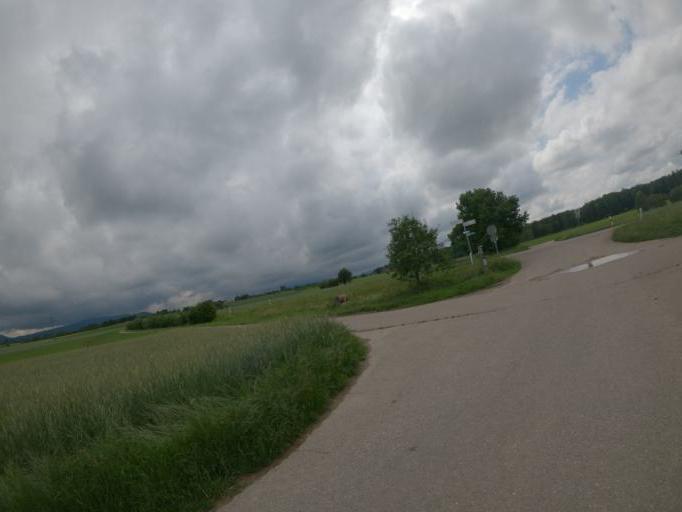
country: DE
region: Baden-Wuerttemberg
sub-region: Regierungsbezirk Stuttgart
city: Albershausen
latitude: 48.6758
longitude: 9.5555
